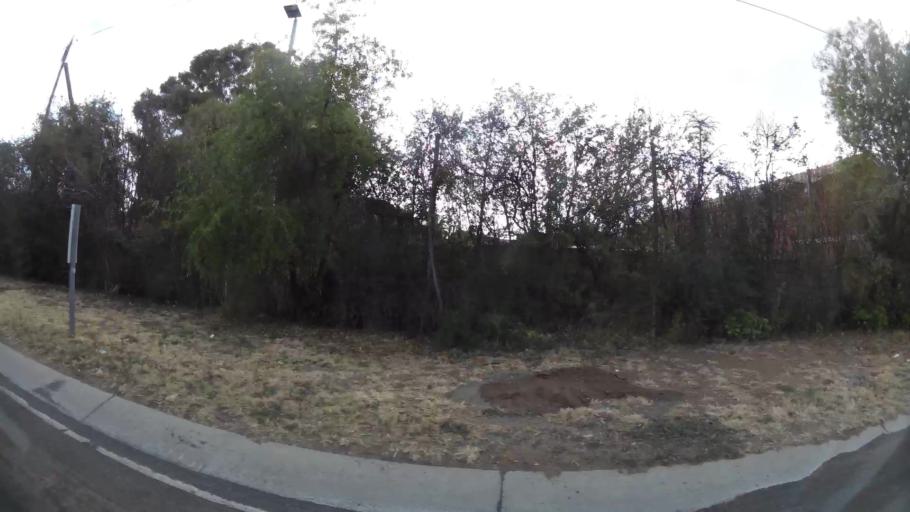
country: ZA
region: Orange Free State
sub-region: Mangaung Metropolitan Municipality
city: Bloemfontein
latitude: -29.0820
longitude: 26.1957
